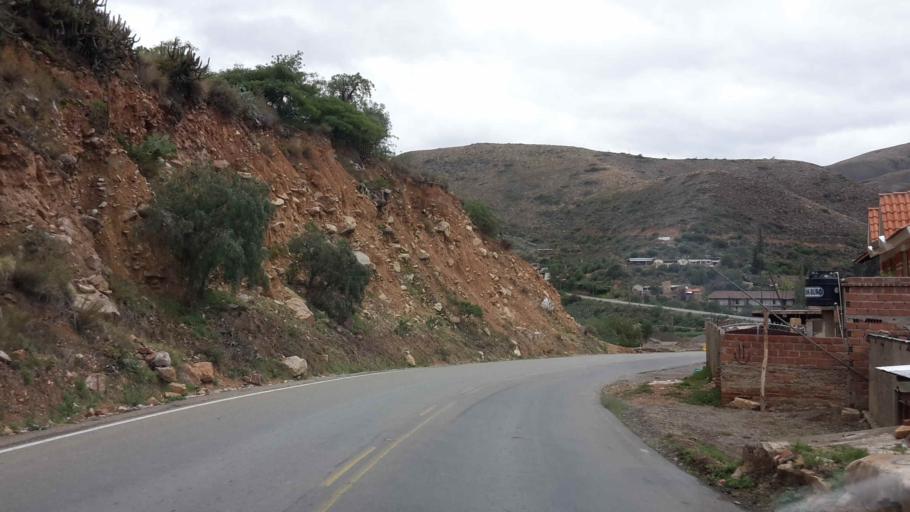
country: BO
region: Cochabamba
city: Punata
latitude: -17.5072
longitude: -65.8027
